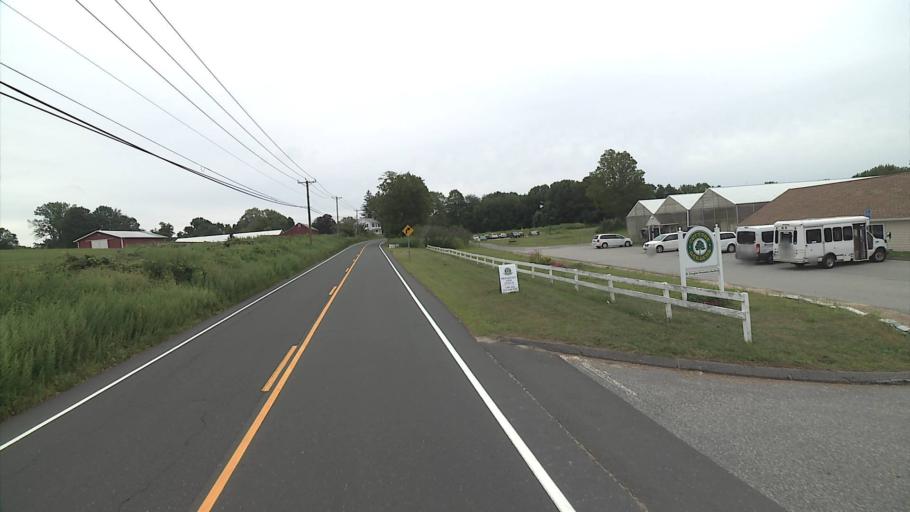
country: US
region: Connecticut
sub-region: New London County
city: Colchester
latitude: 41.5339
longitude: -72.2991
